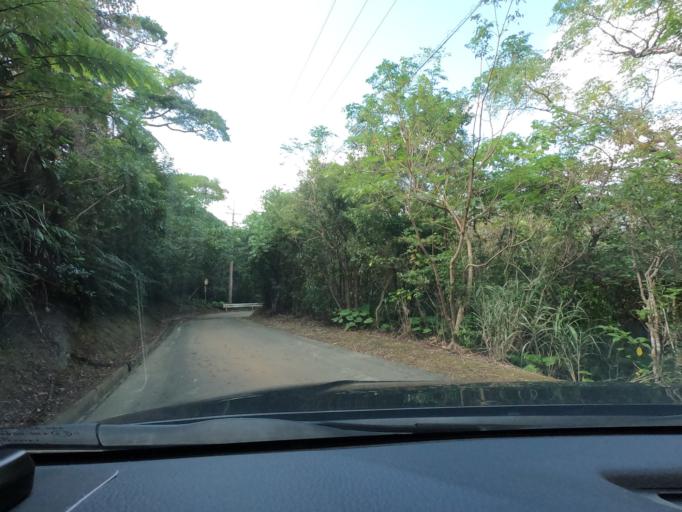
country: JP
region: Okinawa
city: Nago
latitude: 26.7555
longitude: 128.2008
